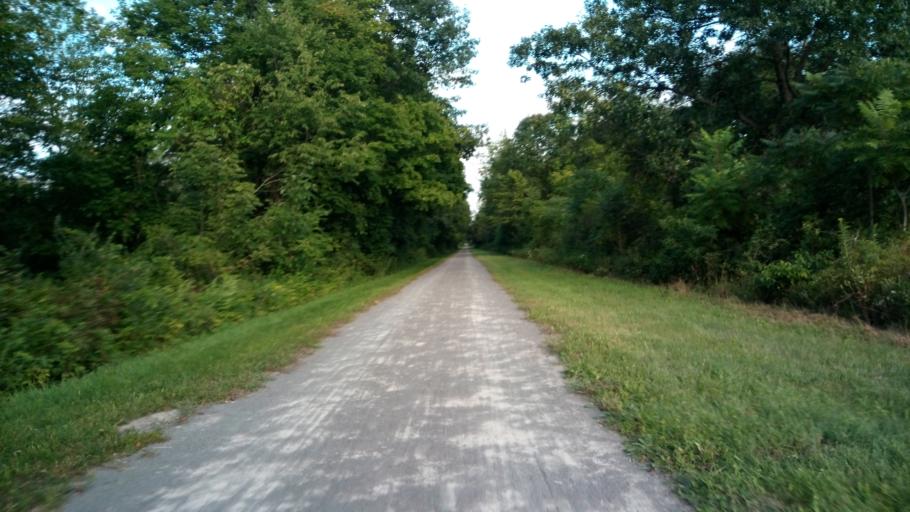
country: US
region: New York
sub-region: Ontario County
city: Victor
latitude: 43.0016
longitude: -77.4676
